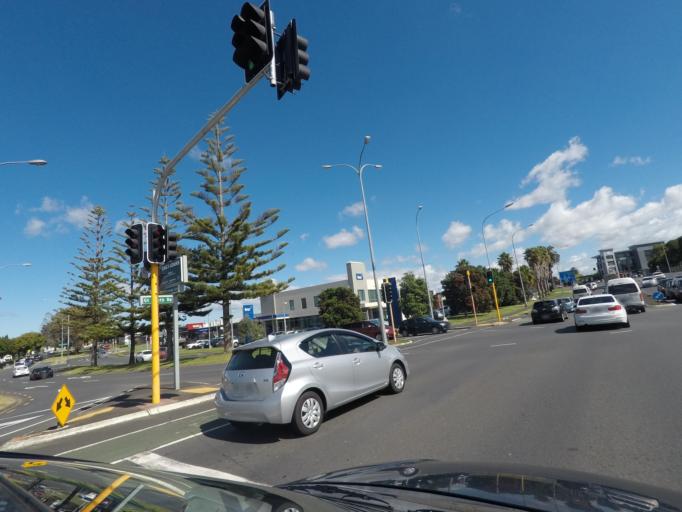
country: NZ
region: Auckland
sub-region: Auckland
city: Manukau City
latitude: -36.9896
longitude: 174.8831
